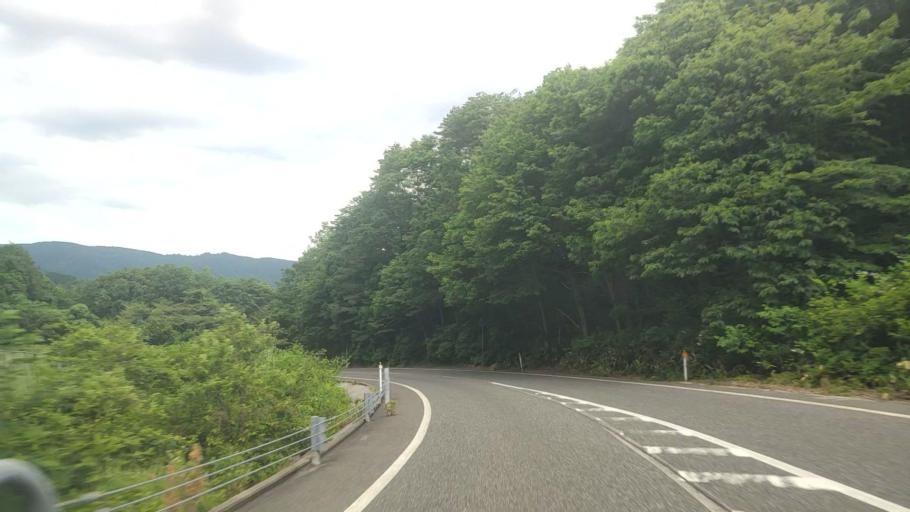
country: JP
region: Tottori
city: Kurayoshi
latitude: 35.2929
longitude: 133.9913
